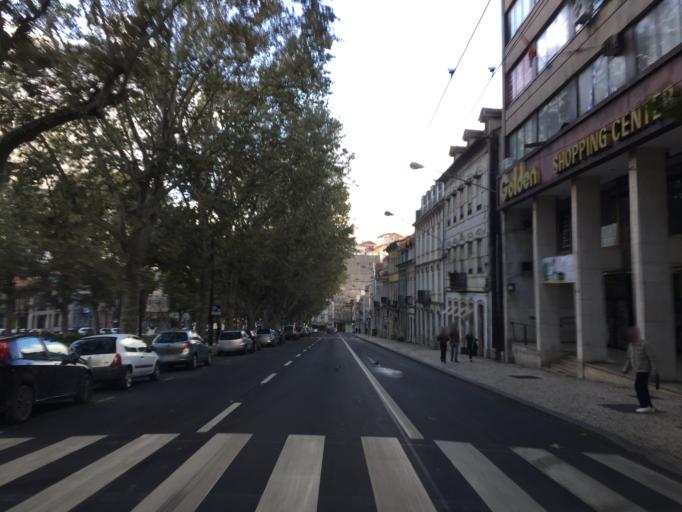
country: PT
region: Coimbra
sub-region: Coimbra
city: Coimbra
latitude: 40.2102
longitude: -8.4207
